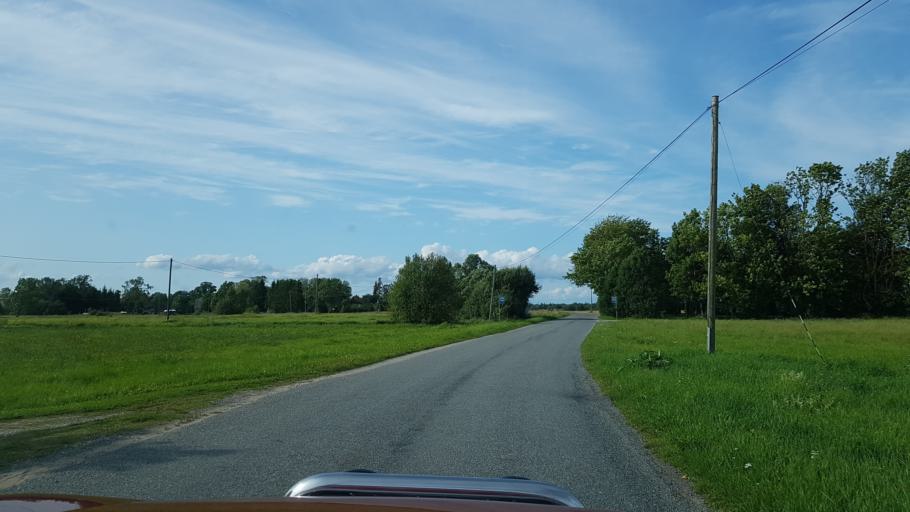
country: EE
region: Laeaene
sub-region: Lihula vald
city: Lihula
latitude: 58.4462
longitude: 24.0021
